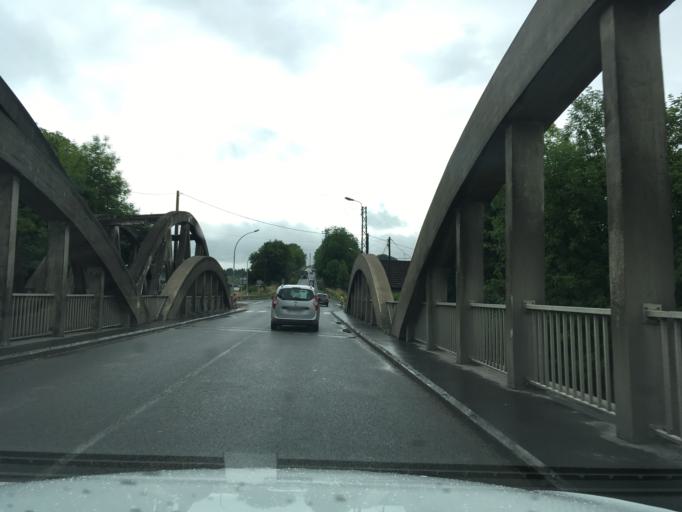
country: FR
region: Picardie
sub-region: Departement de l'Aisne
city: Origny-Sainte-Benoite
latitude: 49.8396
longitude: 3.4792
